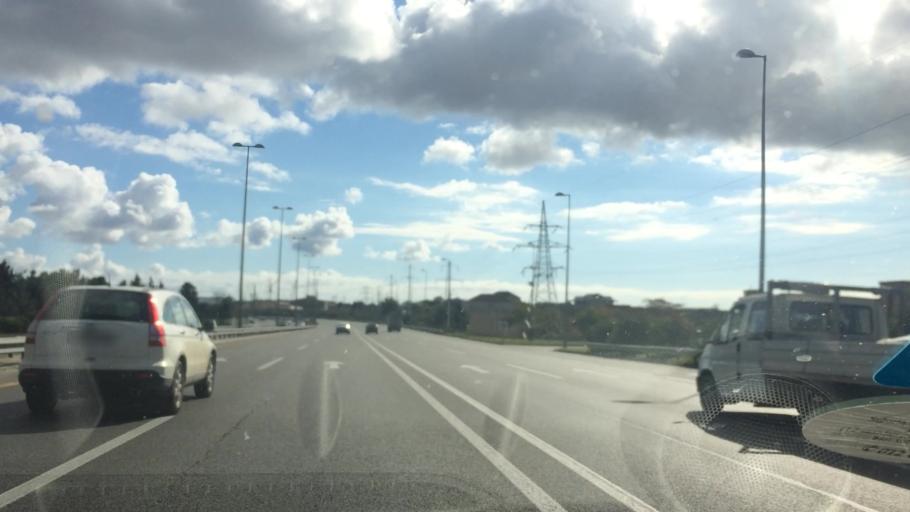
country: AZ
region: Baki
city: Ramana
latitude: 40.4402
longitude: 49.9745
